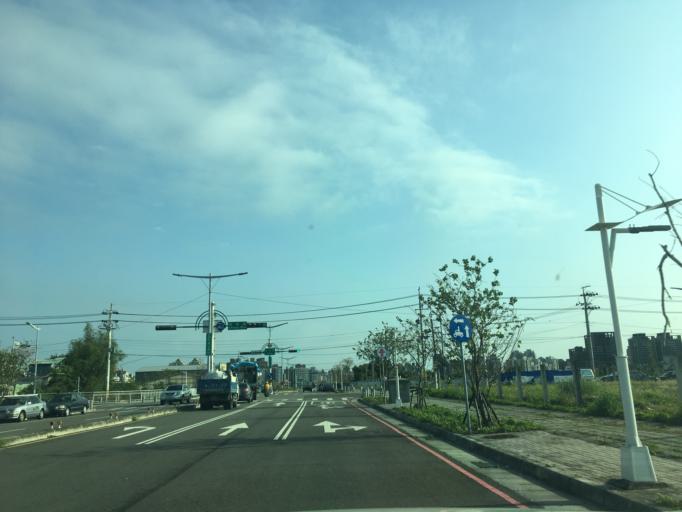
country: TW
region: Taiwan
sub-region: Taichung City
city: Taichung
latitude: 24.1935
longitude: 120.6934
